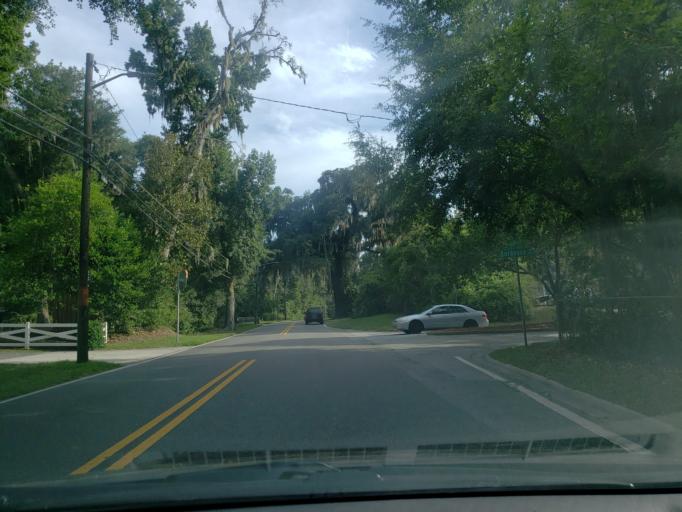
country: US
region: Georgia
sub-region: Chatham County
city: Montgomery
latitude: 31.9620
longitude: -81.1362
